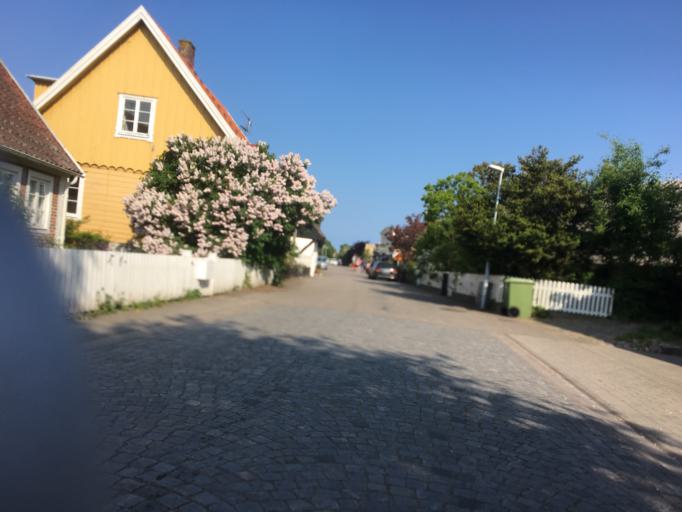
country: SE
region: Skane
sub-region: Hoganas Kommun
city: Hoganas
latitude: 56.1447
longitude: 12.5754
